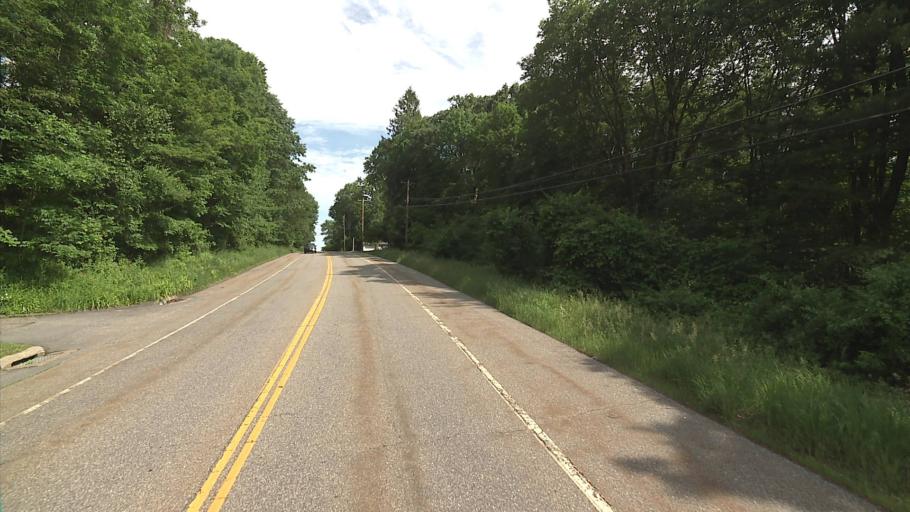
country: US
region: Connecticut
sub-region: Litchfield County
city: Litchfield
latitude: 41.7683
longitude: -73.1984
